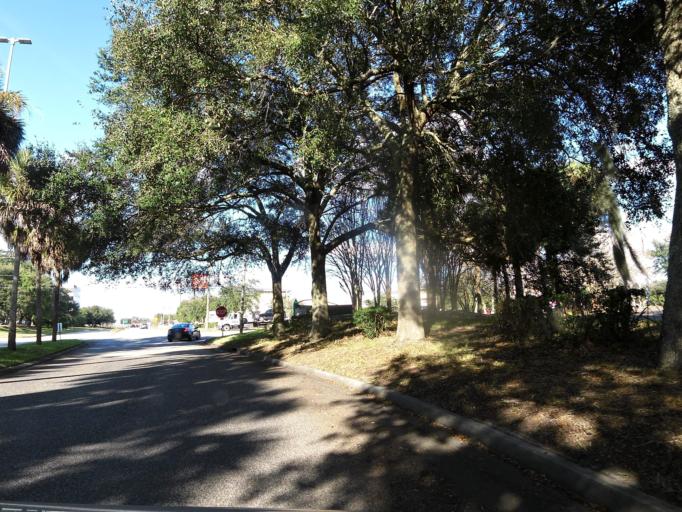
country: US
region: Florida
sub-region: Duval County
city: Jacksonville
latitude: 30.3256
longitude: -81.5515
